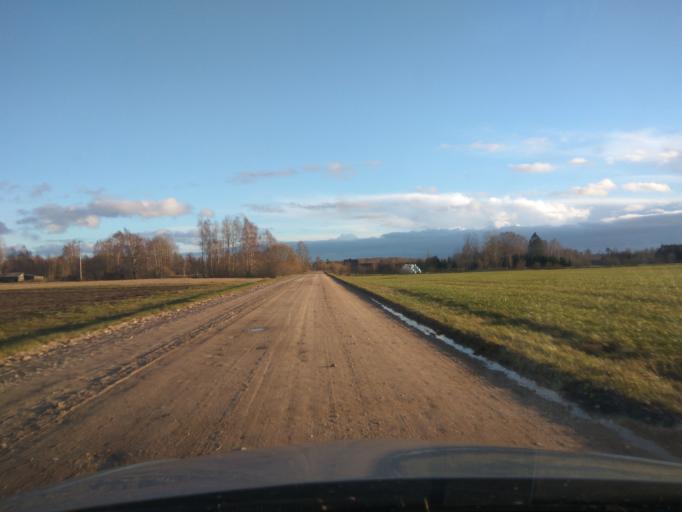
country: LV
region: Aizpute
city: Aizpute
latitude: 56.7621
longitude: 21.7166
